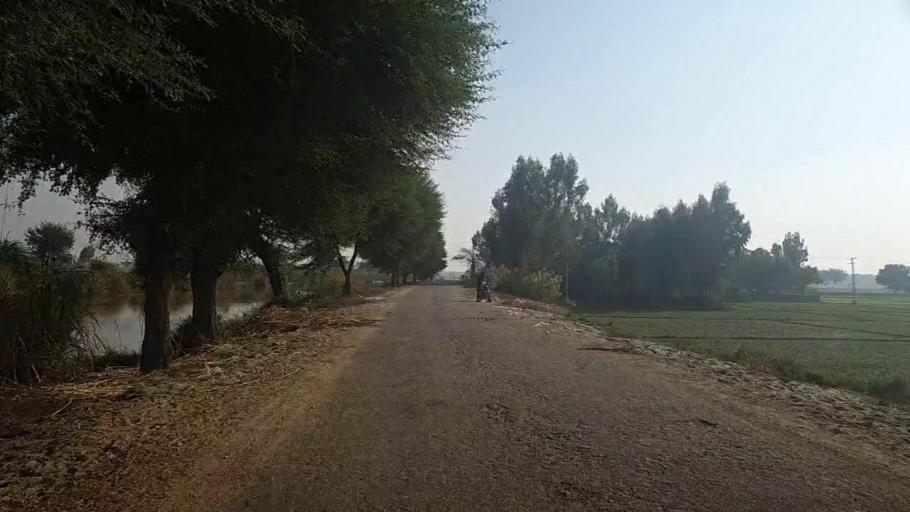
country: PK
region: Sindh
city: Bozdar
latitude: 27.2513
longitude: 68.6772
